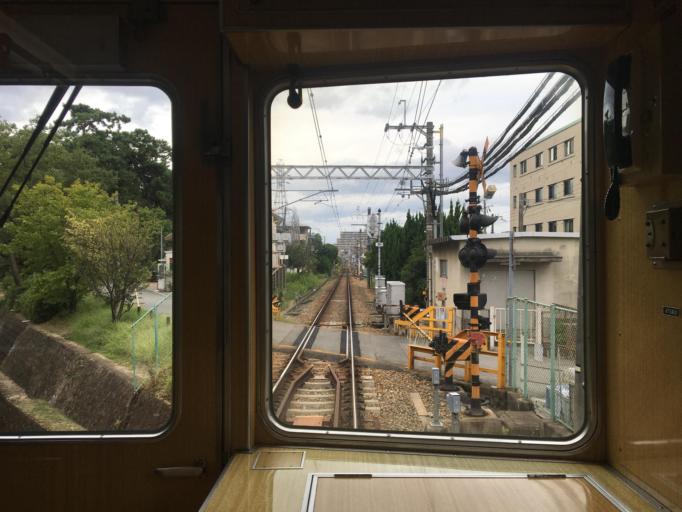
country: JP
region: Hyogo
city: Ashiya
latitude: 34.7494
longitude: 135.3288
